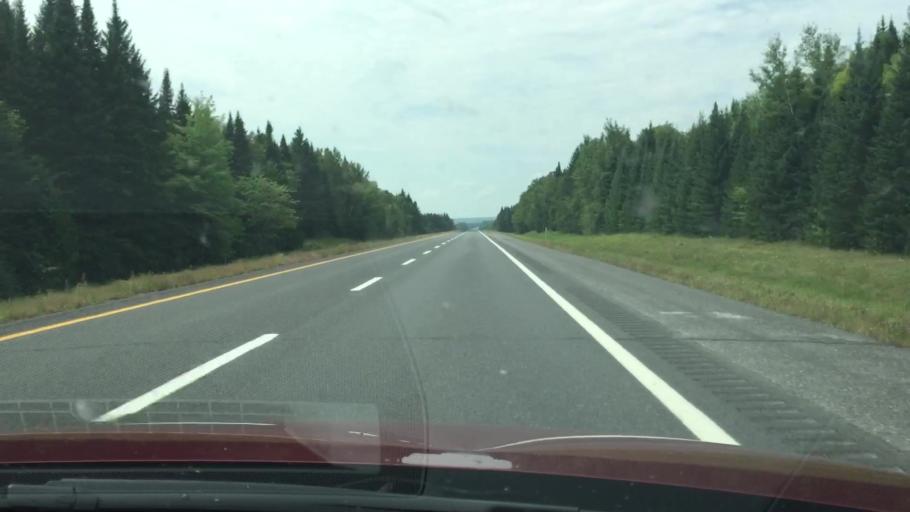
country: US
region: Maine
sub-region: Aroostook County
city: Houlton
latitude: 46.1414
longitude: -67.9660
